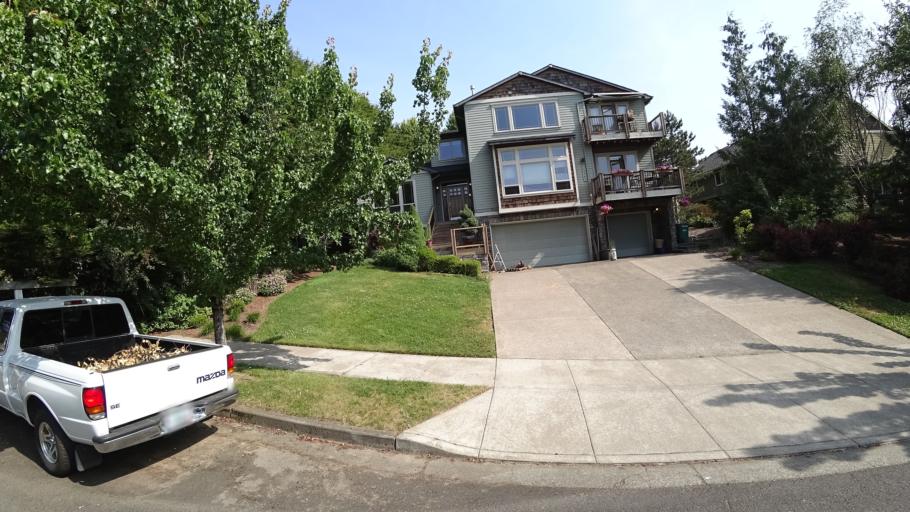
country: US
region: Oregon
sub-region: Clackamas County
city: Happy Valley
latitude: 45.4551
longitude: -122.5222
